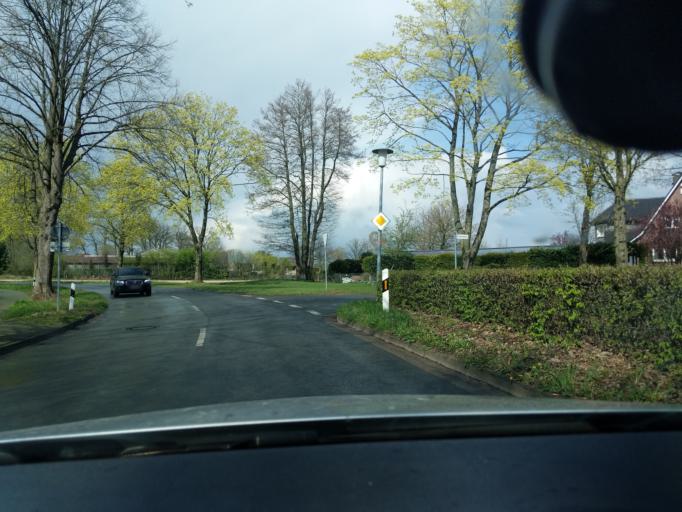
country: DE
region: Lower Saxony
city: Bargstedt
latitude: 53.4572
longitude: 9.4531
